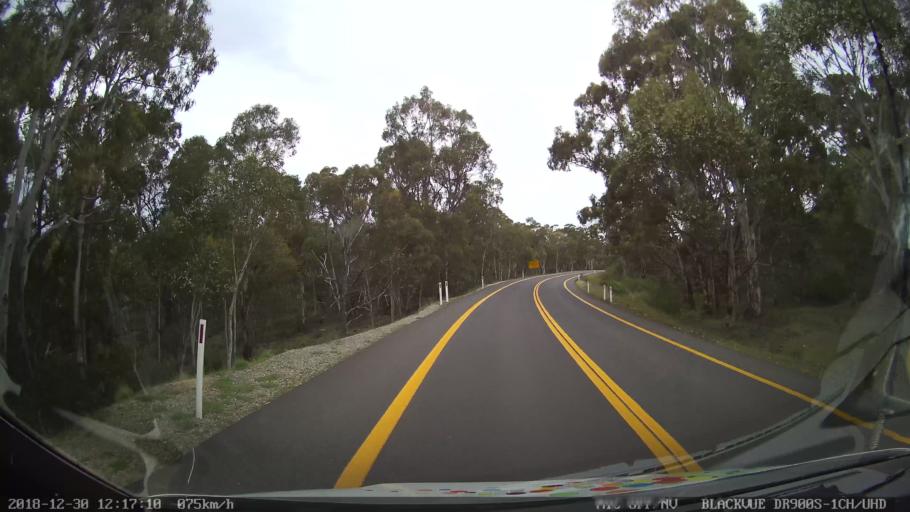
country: AU
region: New South Wales
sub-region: Snowy River
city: Jindabyne
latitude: -36.3525
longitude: 148.5635
